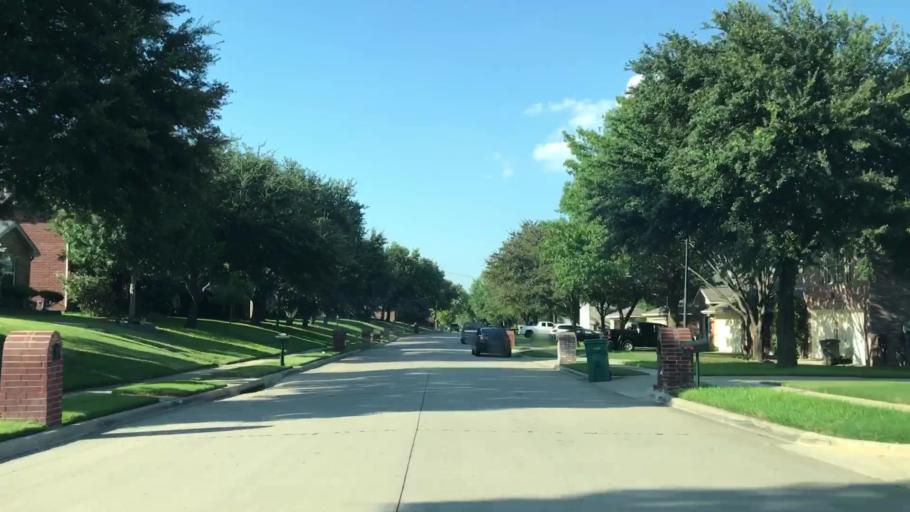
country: US
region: Texas
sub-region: Denton County
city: Lewisville
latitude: 33.0091
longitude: -97.0112
